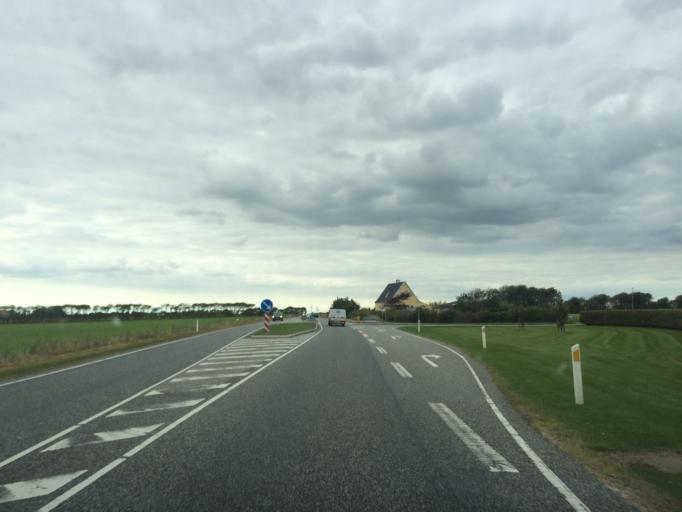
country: DK
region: Central Jutland
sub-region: Ringkobing-Skjern Kommune
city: Skjern
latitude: 56.0562
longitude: 8.3919
